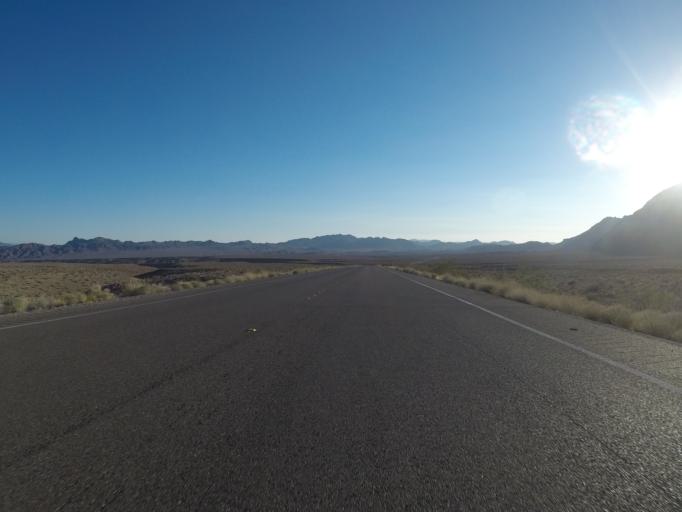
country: US
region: Nevada
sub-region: Clark County
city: Moapa Valley
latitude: 36.3520
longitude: -114.4832
